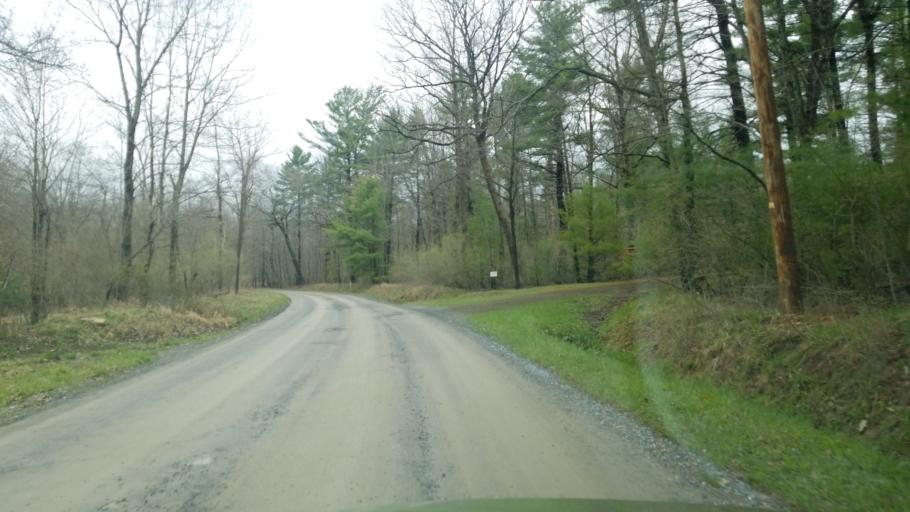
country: US
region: Pennsylvania
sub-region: Clearfield County
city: Shiloh
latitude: 41.1410
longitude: -78.3331
